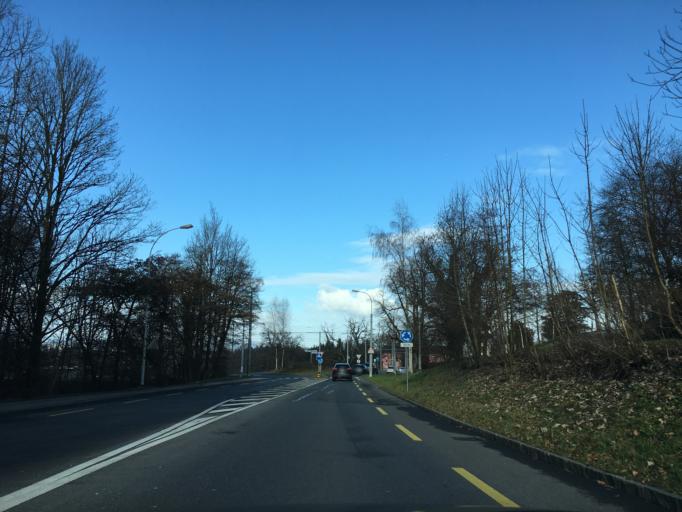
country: CH
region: Lucerne
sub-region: Lucerne-Land District
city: Ebikon
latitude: 47.0651
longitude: 8.3235
